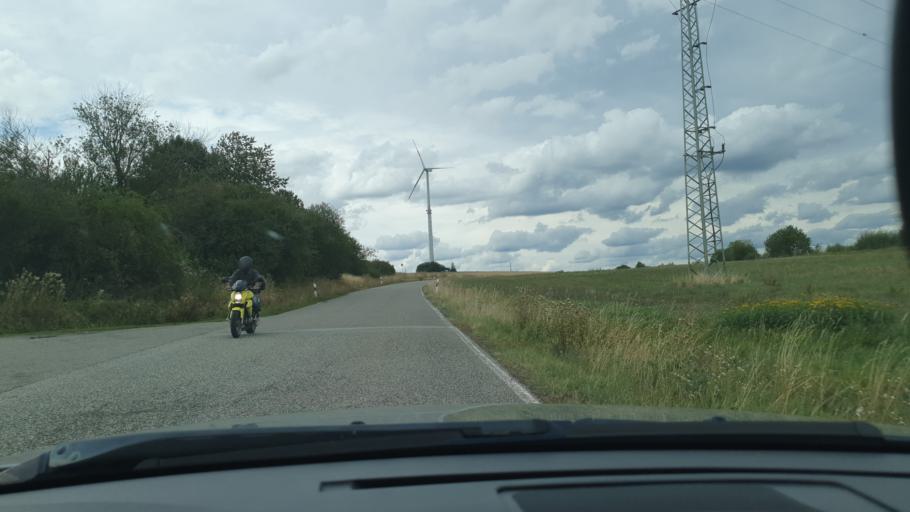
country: DE
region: Rheinland-Pfalz
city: Bann
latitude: 49.3776
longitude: 7.6053
